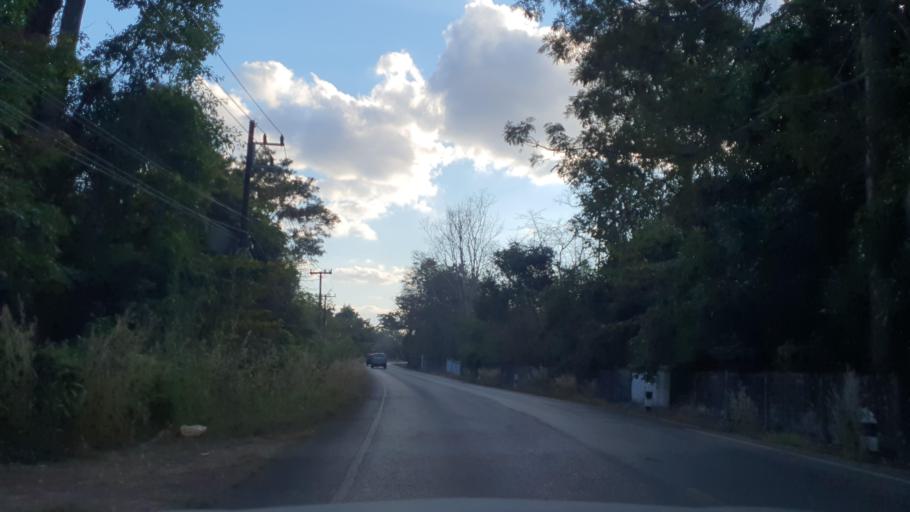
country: TH
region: Changwat Bueng Kan
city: Si Wilai
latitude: 18.1329
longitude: 103.8849
